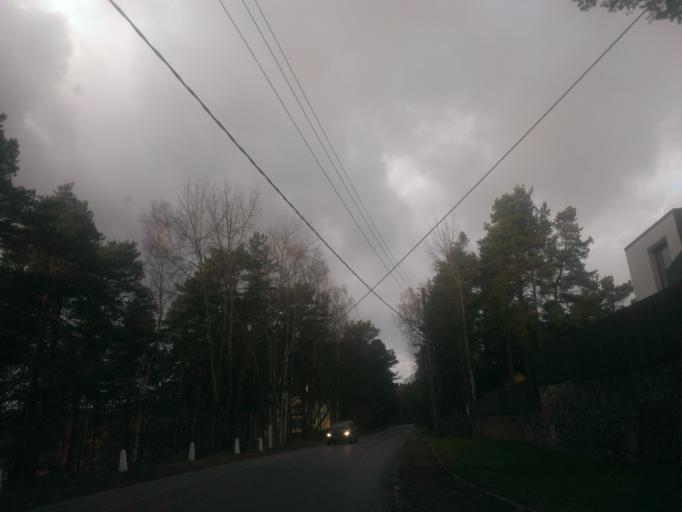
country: LV
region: Riga
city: Bergi
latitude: 56.9857
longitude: 24.2970
